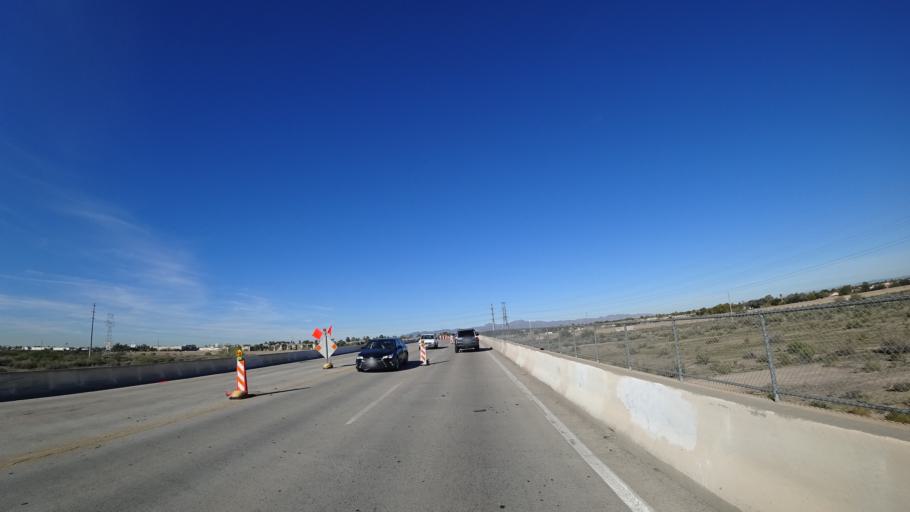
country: US
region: Arizona
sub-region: Maricopa County
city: Avondale
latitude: 33.4620
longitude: -112.3281
